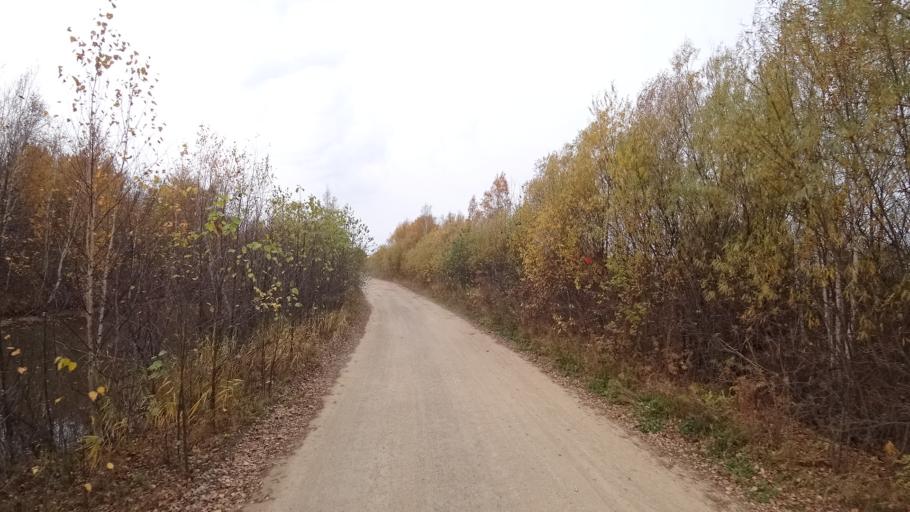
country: RU
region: Khabarovsk Krai
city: Amursk
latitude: 50.1469
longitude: 136.9740
